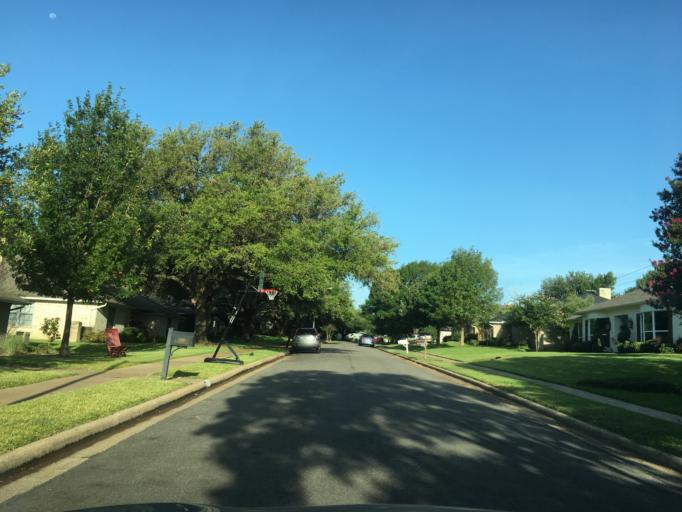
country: US
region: Texas
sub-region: Dallas County
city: Richardson
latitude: 32.8883
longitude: -96.7371
